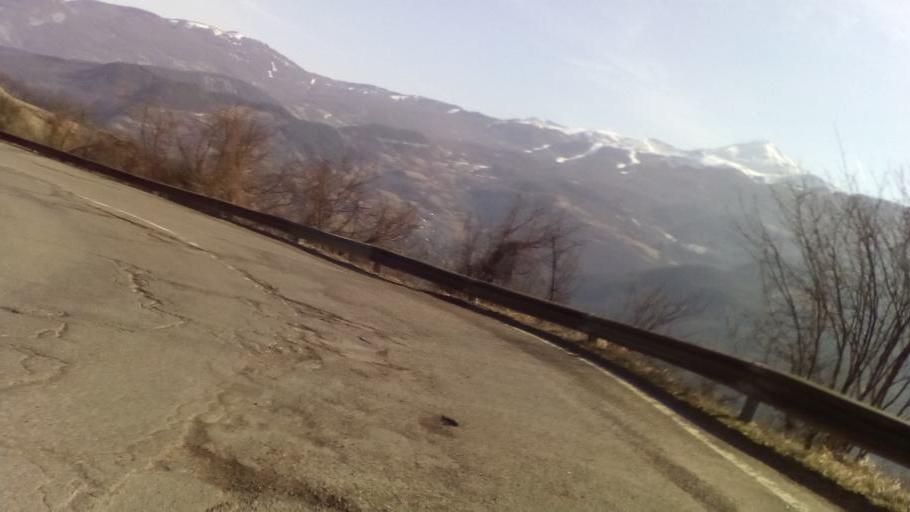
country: IT
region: Emilia-Romagna
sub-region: Provincia di Modena
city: Riolunato
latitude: 44.2383
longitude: 10.6286
